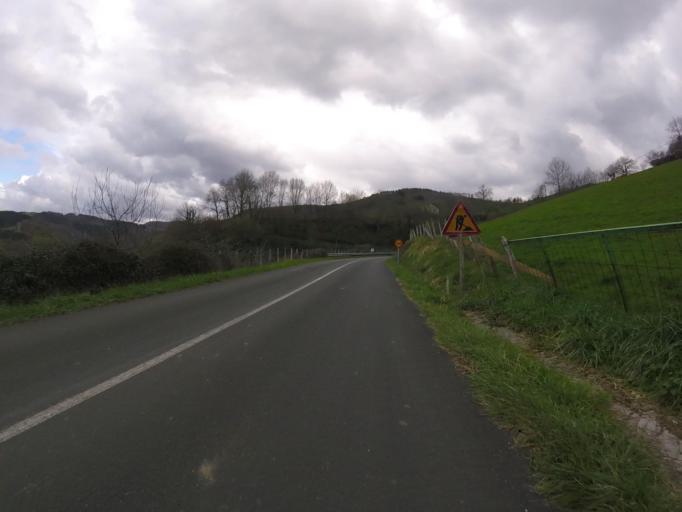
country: ES
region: Basque Country
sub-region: Provincia de Guipuzcoa
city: Errenteria
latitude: 43.2833
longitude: -1.8557
